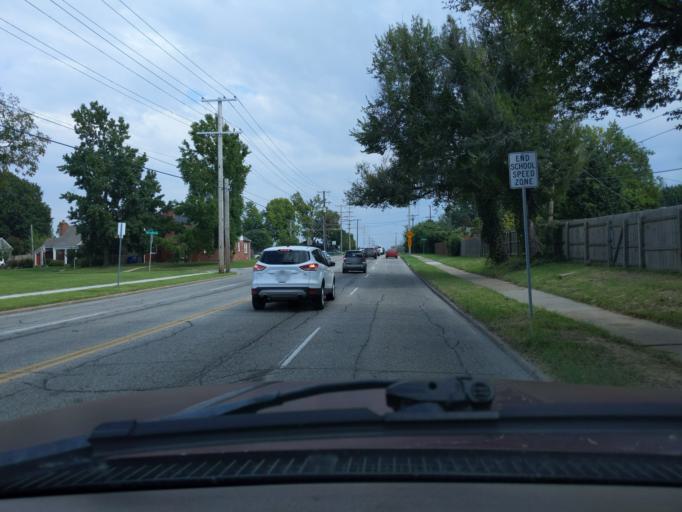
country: US
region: Oklahoma
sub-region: Tulsa County
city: Tulsa
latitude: 36.1334
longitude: -95.9374
